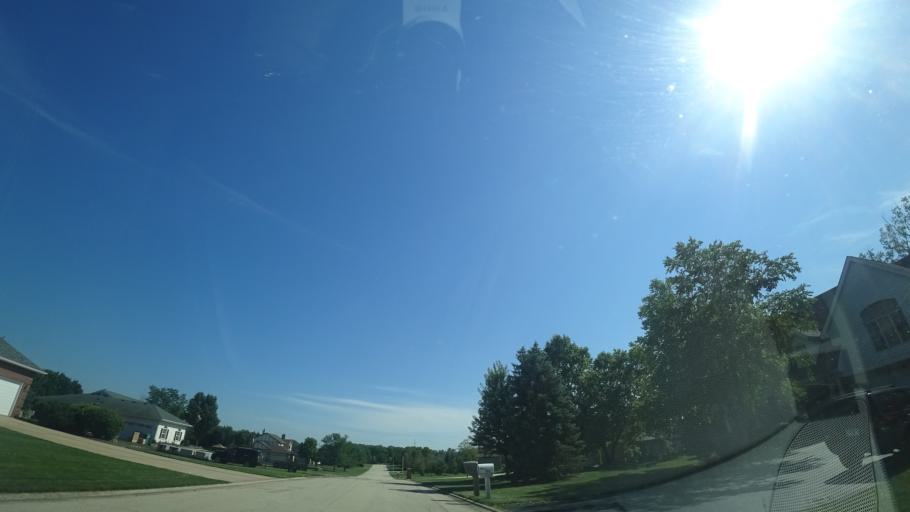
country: US
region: Illinois
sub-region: Will County
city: Homer Glen
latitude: 41.5613
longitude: -87.9180
